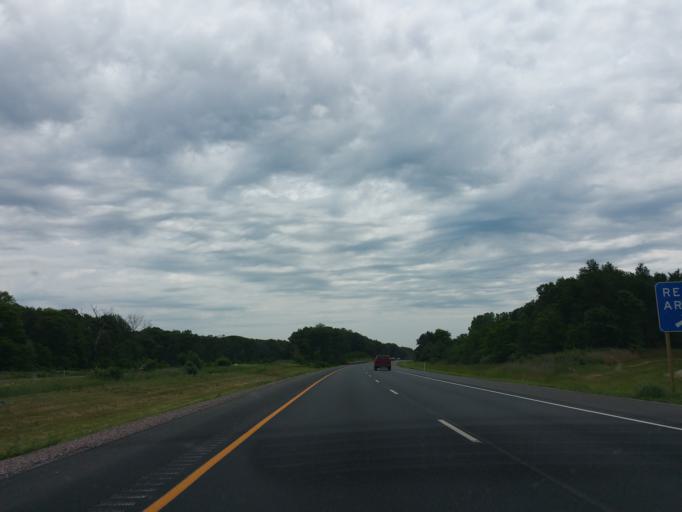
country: US
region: Wisconsin
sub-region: Juneau County
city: Mauston
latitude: 43.7607
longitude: -89.9715
